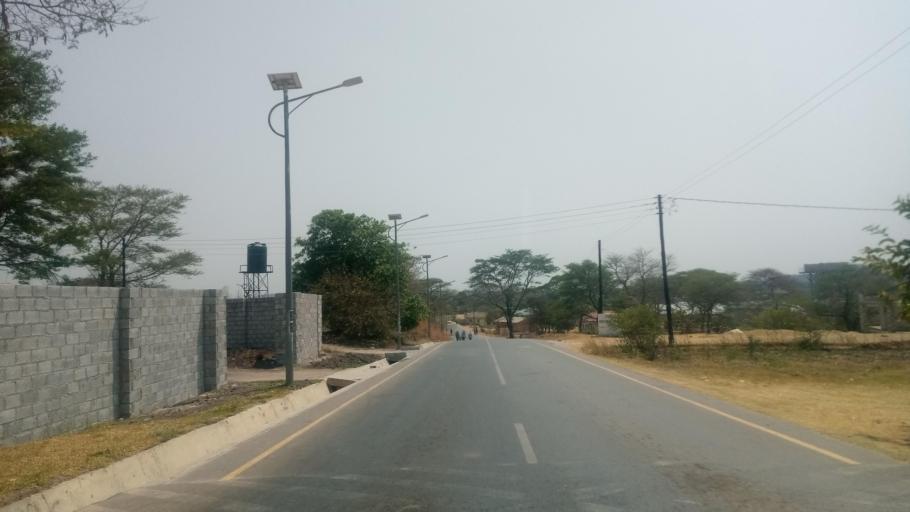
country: ZM
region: Lusaka
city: Lusaka
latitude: -15.4520
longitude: 28.4411
